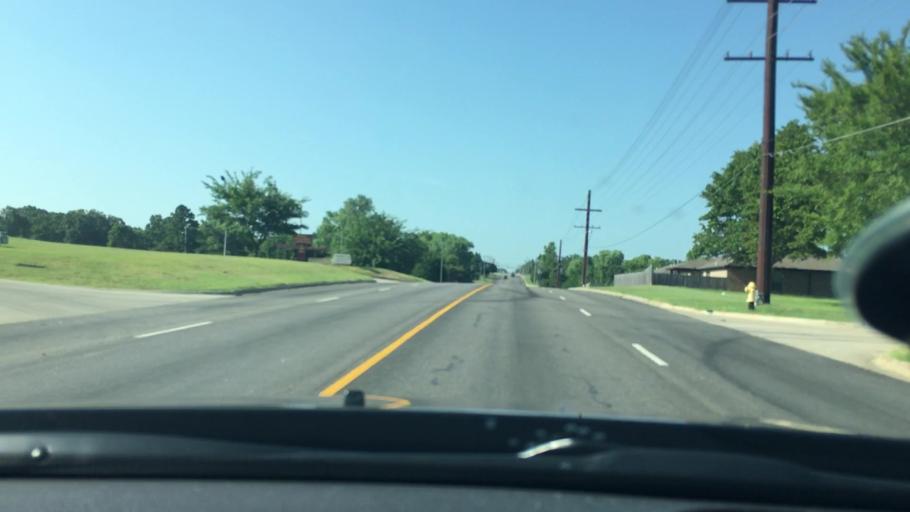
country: US
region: Oklahoma
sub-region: Pontotoc County
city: Ada
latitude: 34.7885
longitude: -96.6348
